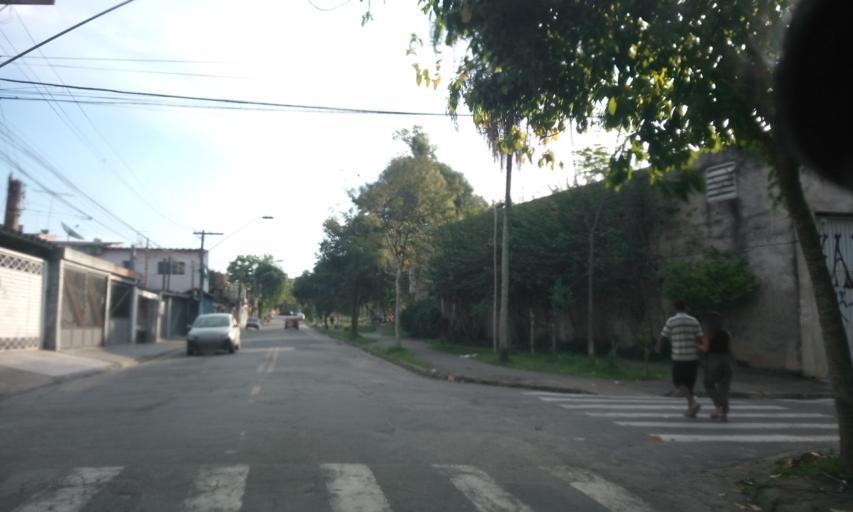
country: BR
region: Sao Paulo
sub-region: Santo Andre
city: Santo Andre
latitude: -23.7053
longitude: -46.5076
